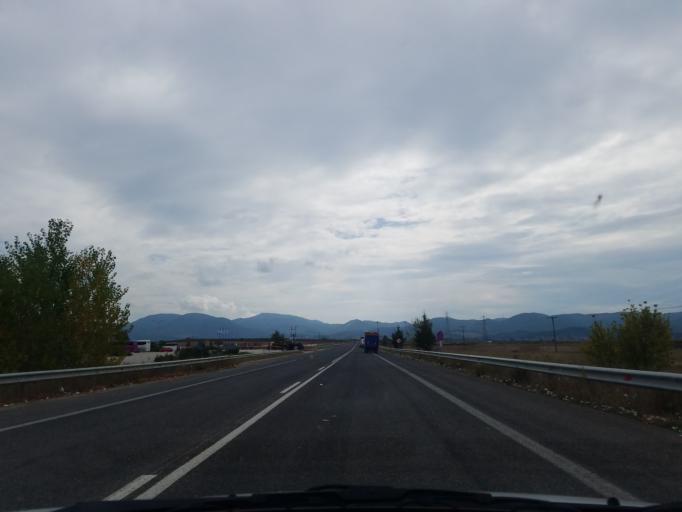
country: GR
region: Central Greece
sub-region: Nomos Fthiotidos
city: Omvriaki
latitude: 39.0687
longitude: 22.3236
